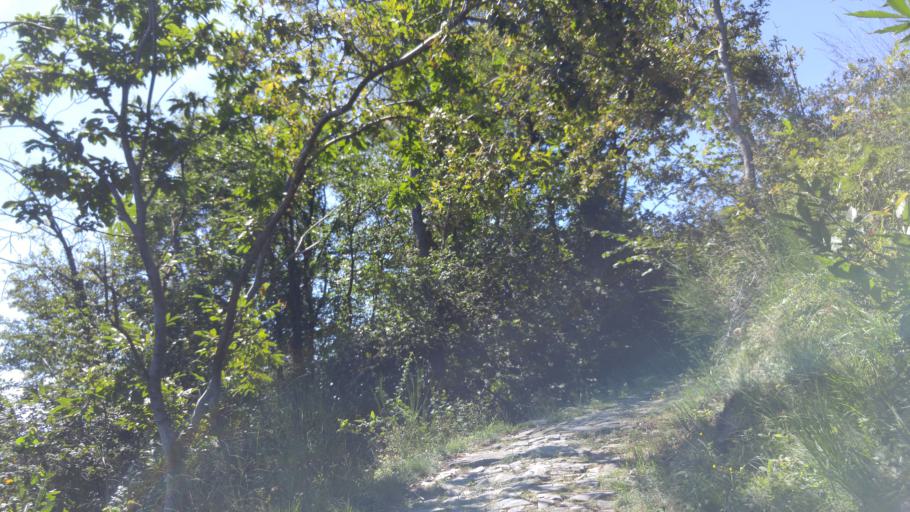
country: IT
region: Piedmont
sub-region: Provincia Verbano-Cusio-Ossola
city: Cannobio
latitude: 46.0743
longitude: 8.6881
